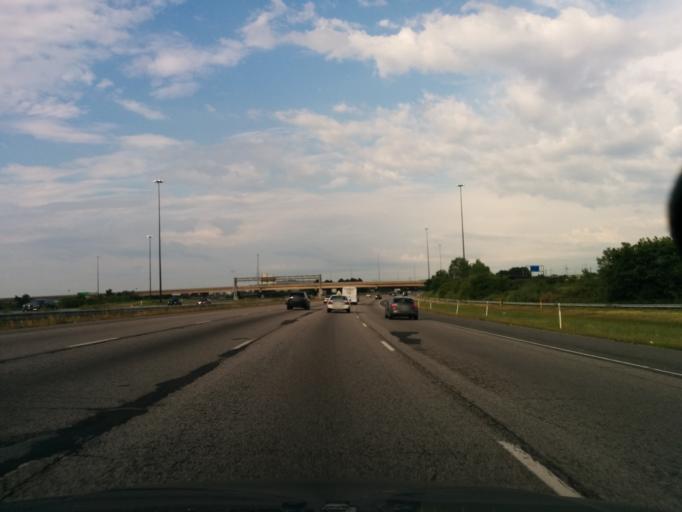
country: US
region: Pennsylvania
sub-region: Delaware County
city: Colwyn
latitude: 39.8794
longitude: -75.2490
